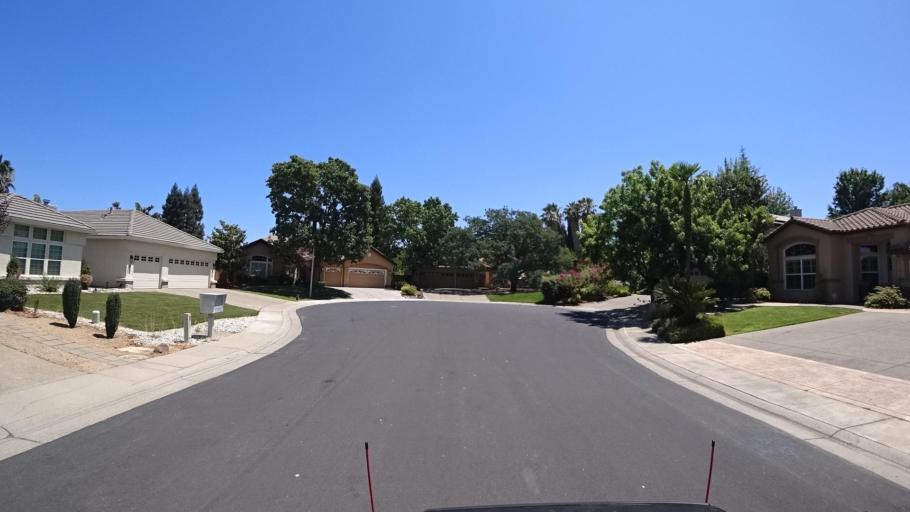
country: US
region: California
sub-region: Placer County
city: Rocklin
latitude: 38.8239
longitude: -121.2510
